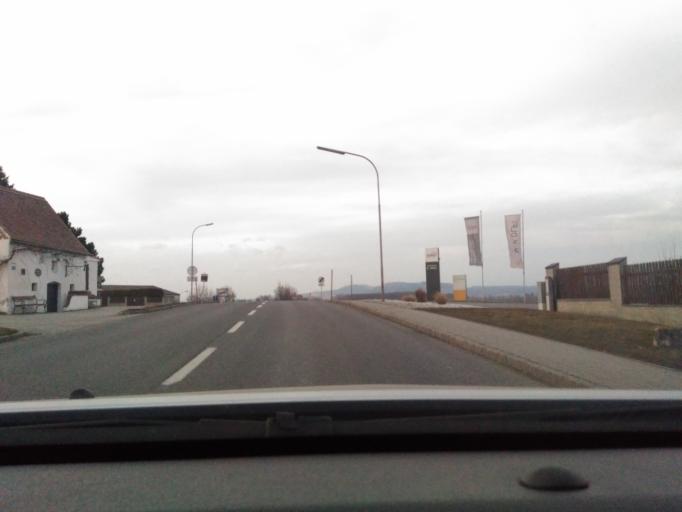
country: AT
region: Lower Austria
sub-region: Politischer Bezirk Mistelbach
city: Drasenhofen
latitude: 48.7595
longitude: 16.6473
